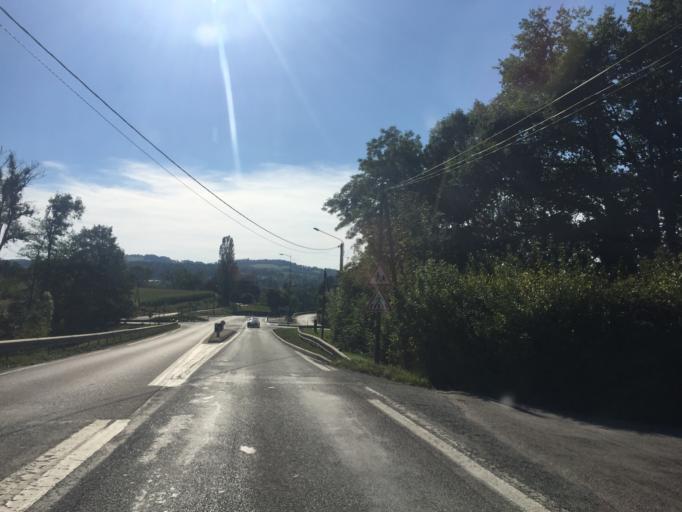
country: FR
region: Rhone-Alpes
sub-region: Departement de la Haute-Savoie
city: Alby-sur-Cheran
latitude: 45.8211
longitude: 6.0348
